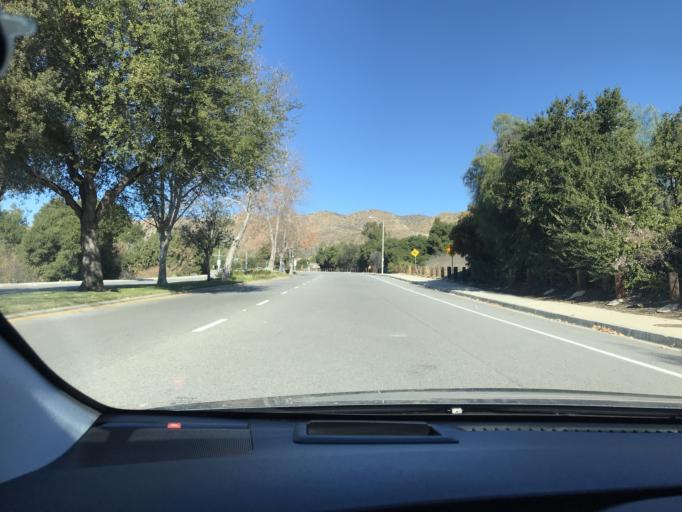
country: US
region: California
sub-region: Ventura County
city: Oak Park
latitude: 34.1780
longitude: -118.7602
